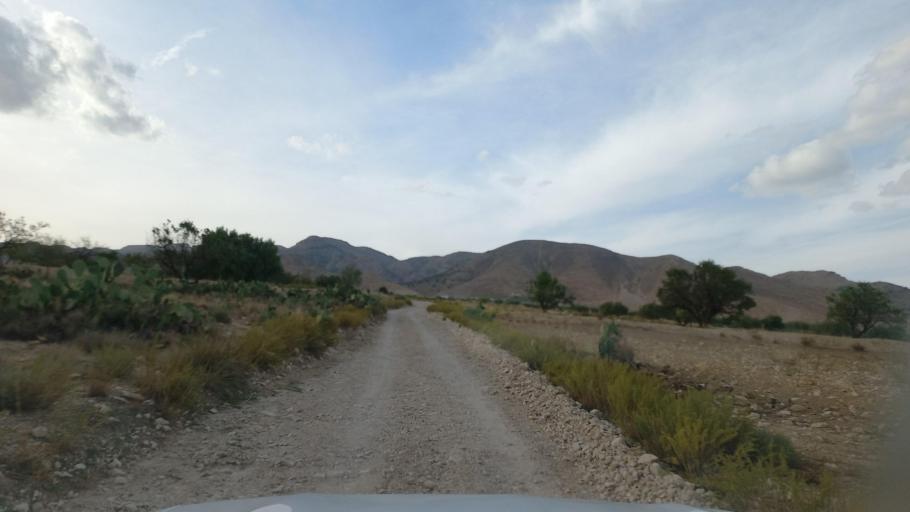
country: TN
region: Al Qasrayn
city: Sbiba
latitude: 35.4439
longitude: 9.0714
